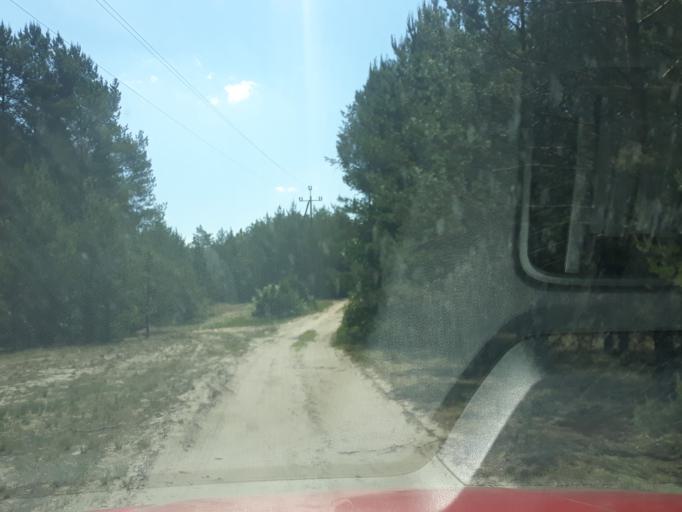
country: PL
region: Pomeranian Voivodeship
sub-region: Powiat chojnicki
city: Chojnice
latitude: 53.8717
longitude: 17.5398
